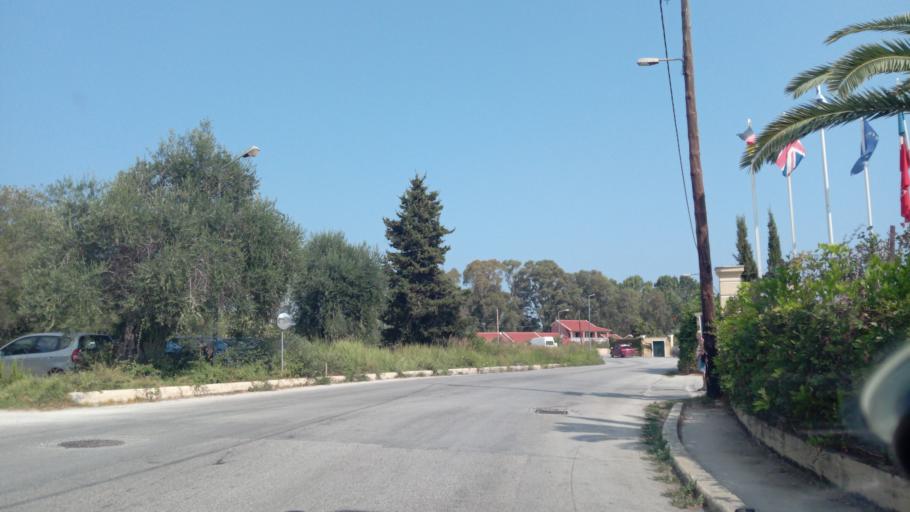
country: GR
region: Ionian Islands
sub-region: Nomos Kerkyras
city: Lefkimmi
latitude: 39.4035
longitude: 20.0968
